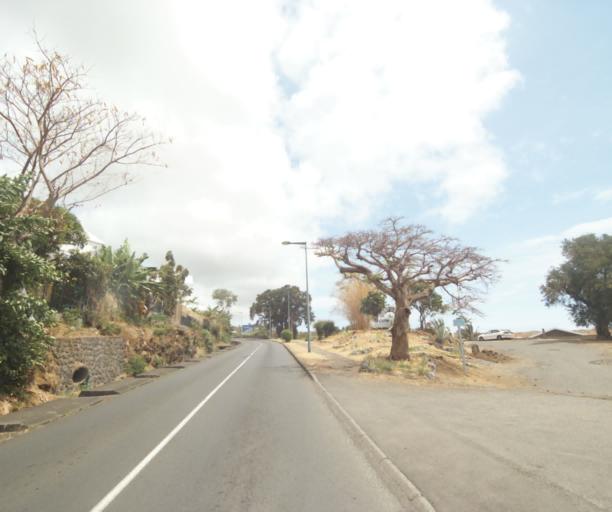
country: RE
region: Reunion
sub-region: Reunion
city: Saint-Paul
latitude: -21.0270
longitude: 55.2653
